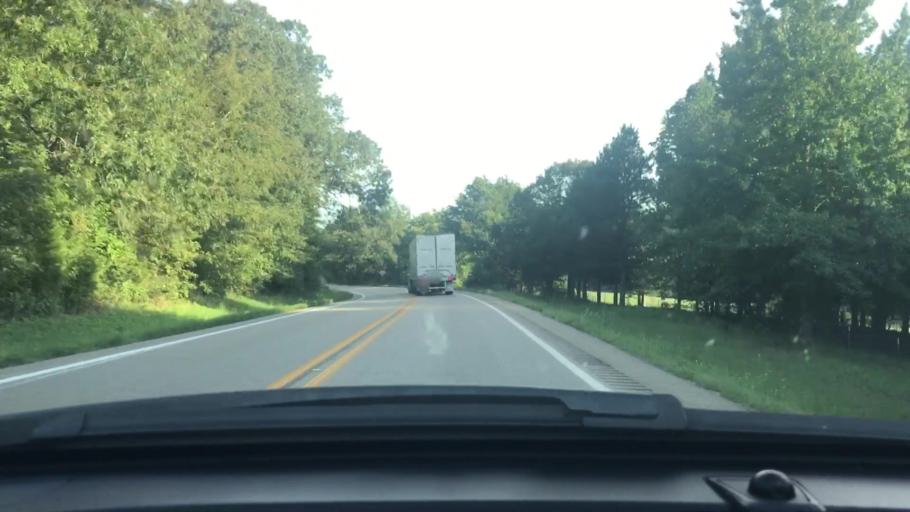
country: US
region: Arkansas
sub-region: Sharp County
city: Cherokee Village
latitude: 36.2414
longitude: -91.2656
